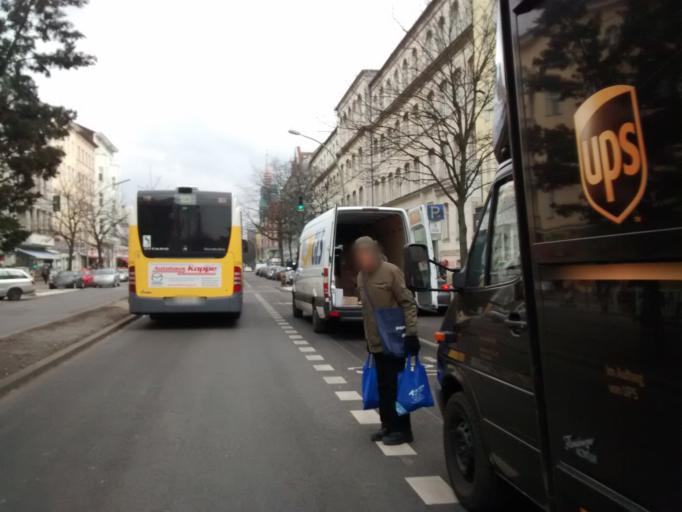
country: DE
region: Berlin
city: Moabit
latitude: 52.5269
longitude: 13.3329
